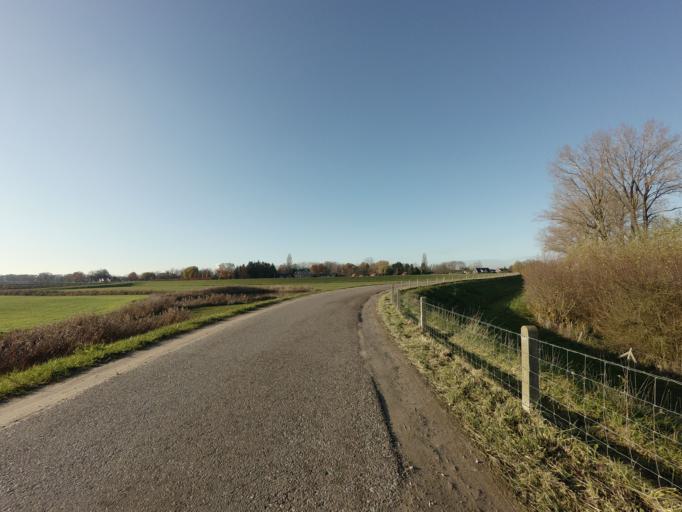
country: NL
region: Gelderland
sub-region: Gemeente Maasdriel
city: Hedel
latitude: 51.7493
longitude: 5.2786
